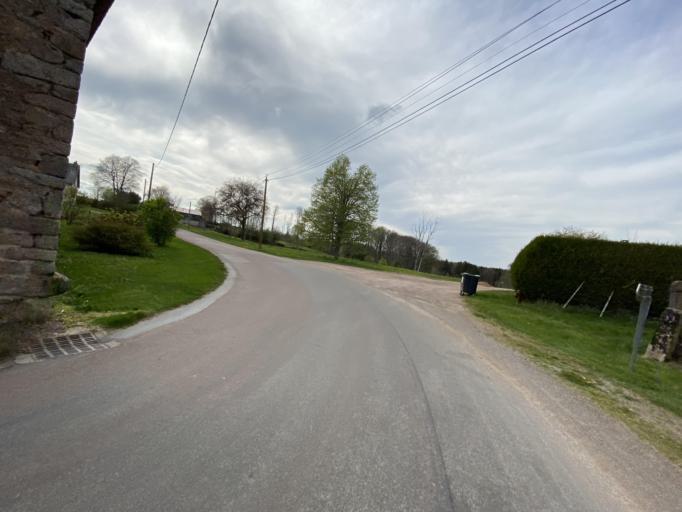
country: FR
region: Bourgogne
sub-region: Departement de la Cote-d'Or
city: Saulieu
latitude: 47.3222
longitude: 4.0802
